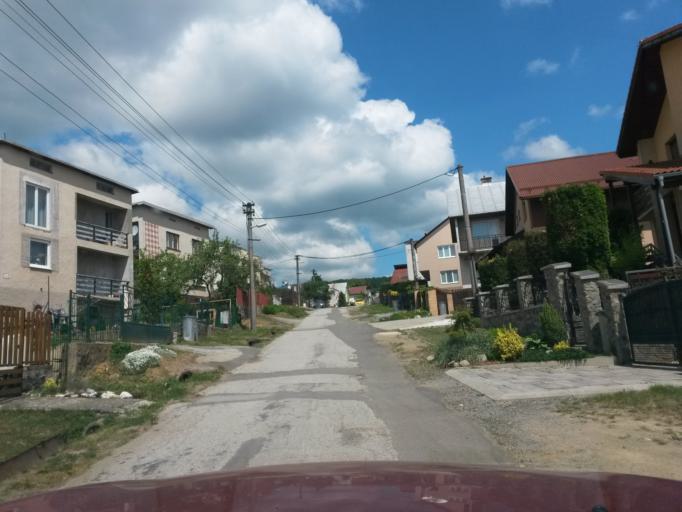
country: SK
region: Kosicky
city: Kosice
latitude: 48.7306
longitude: 21.1407
